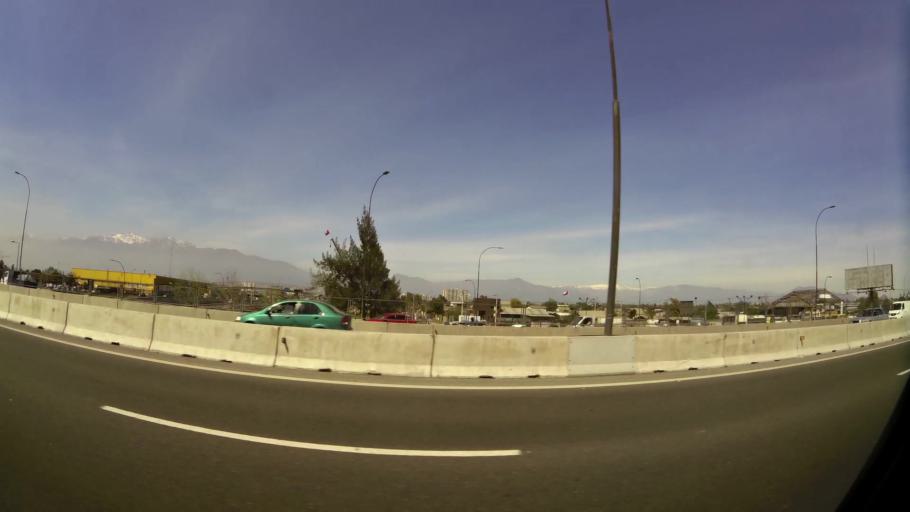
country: CL
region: Santiago Metropolitan
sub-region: Provincia de Maipo
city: San Bernardo
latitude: -33.5327
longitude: -70.6820
